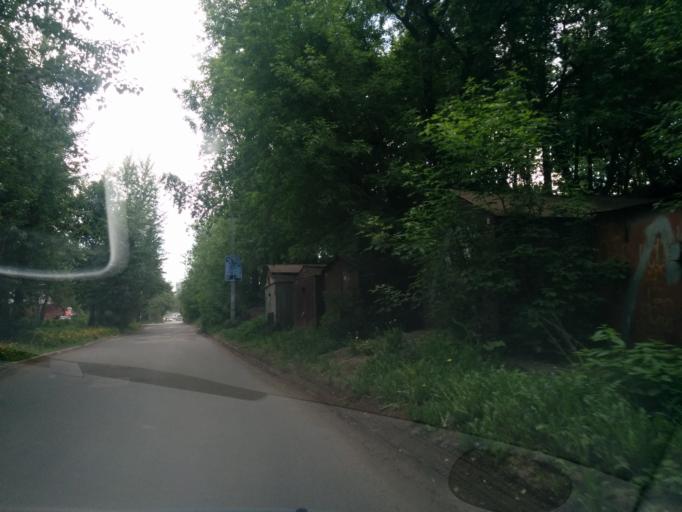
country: RU
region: Perm
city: Perm
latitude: 57.9939
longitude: 56.2055
